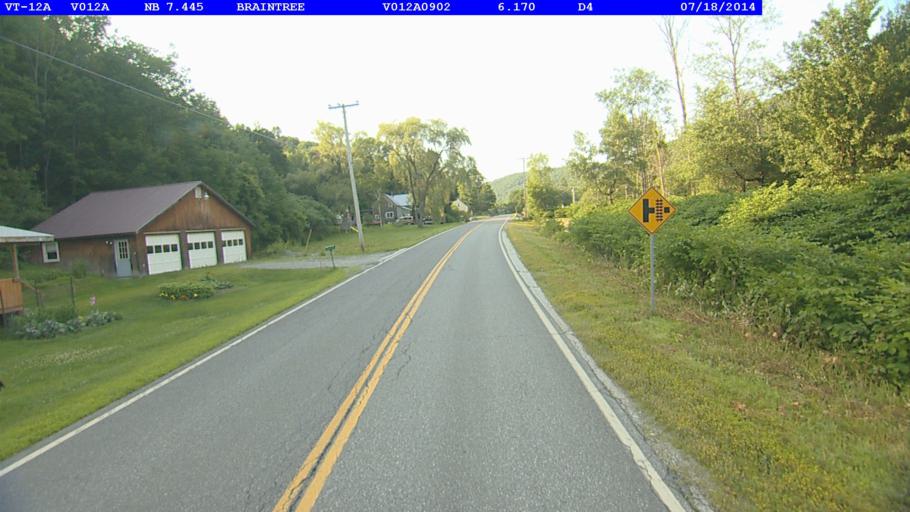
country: US
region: Vermont
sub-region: Orange County
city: Randolph
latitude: 43.9961
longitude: -72.7525
